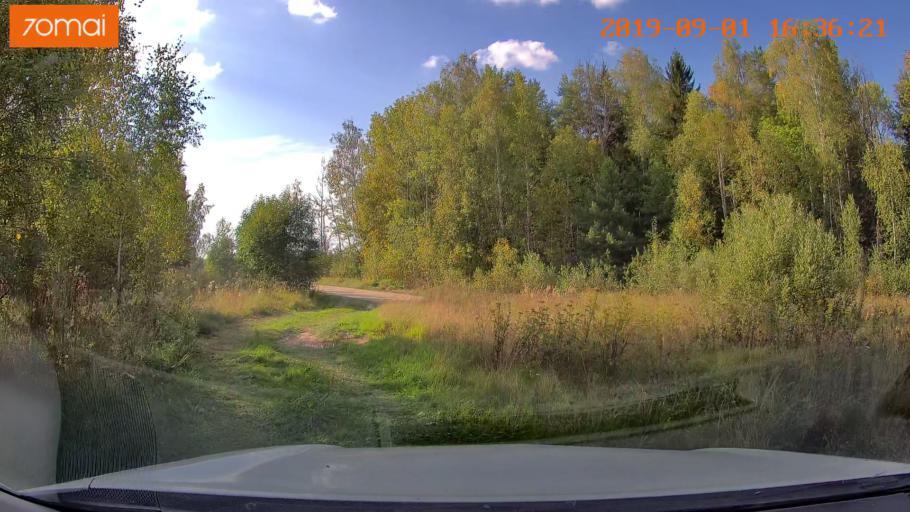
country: RU
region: Kaluga
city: Maloyaroslavets
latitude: 54.9477
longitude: 36.4766
